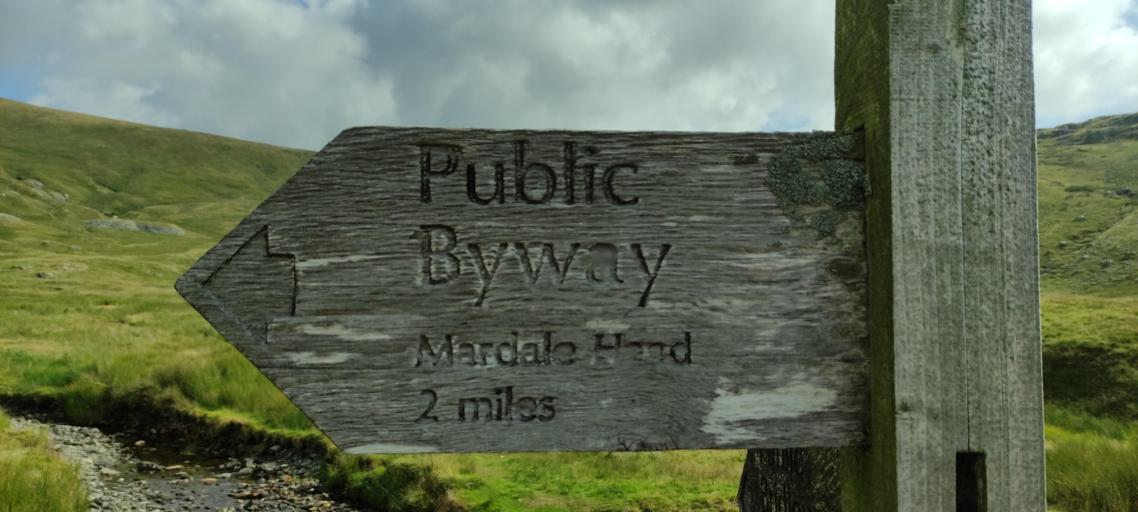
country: GB
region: England
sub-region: Cumbria
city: Windermere
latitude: 54.4687
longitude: -2.8065
